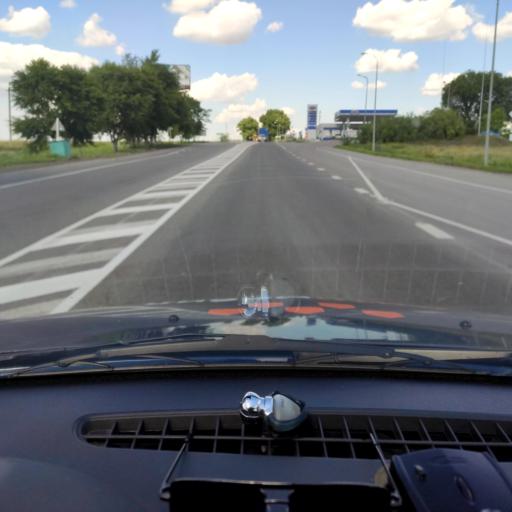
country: RU
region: Voronezj
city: Novovoronezh
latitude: 51.3408
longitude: 39.2744
